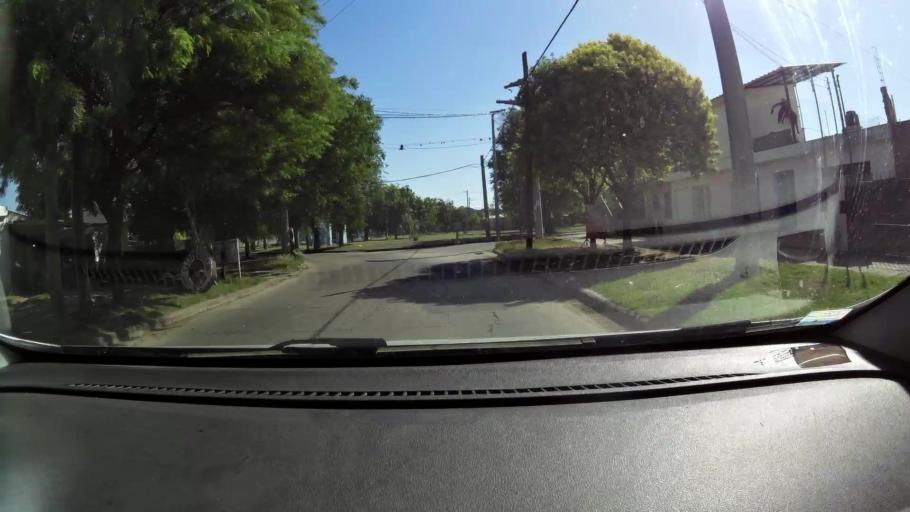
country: AR
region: Cordoba
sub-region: Departamento de Capital
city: Cordoba
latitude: -31.3649
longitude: -64.1721
